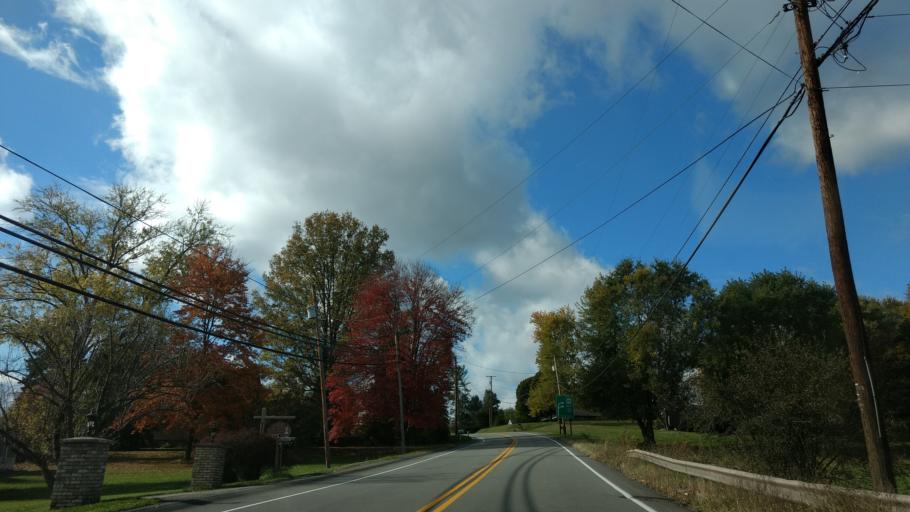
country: US
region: Pennsylvania
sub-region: Westmoreland County
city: Lynnwood-Pricedale
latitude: 40.1467
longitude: -79.8368
